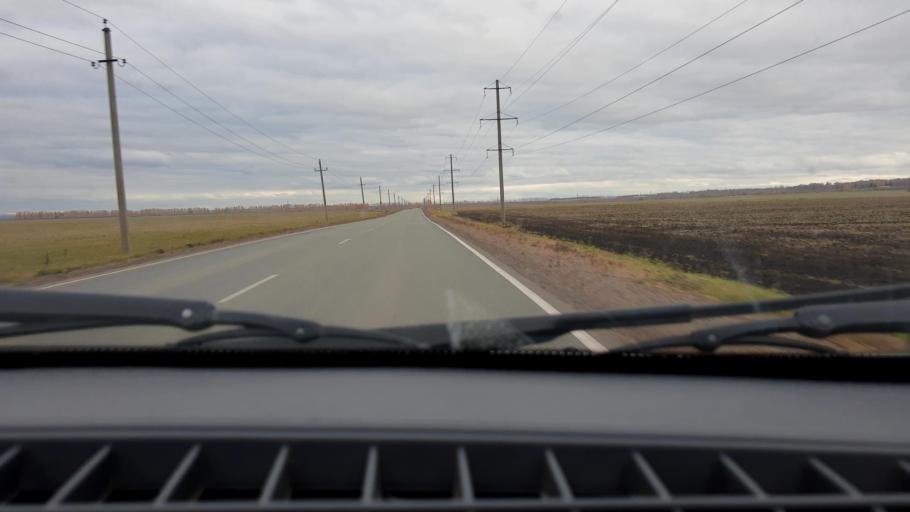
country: RU
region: Bashkortostan
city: Kabakovo
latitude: 54.5433
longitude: 56.0496
